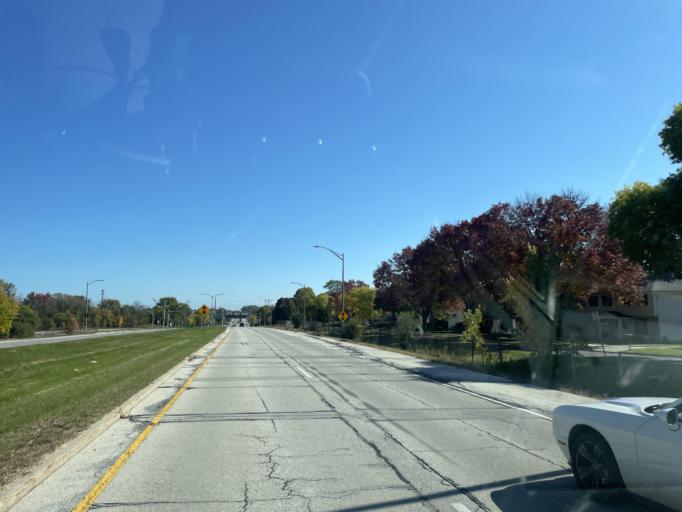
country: US
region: Wisconsin
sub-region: Waukesha County
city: Butler
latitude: 43.1285
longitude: -88.0475
